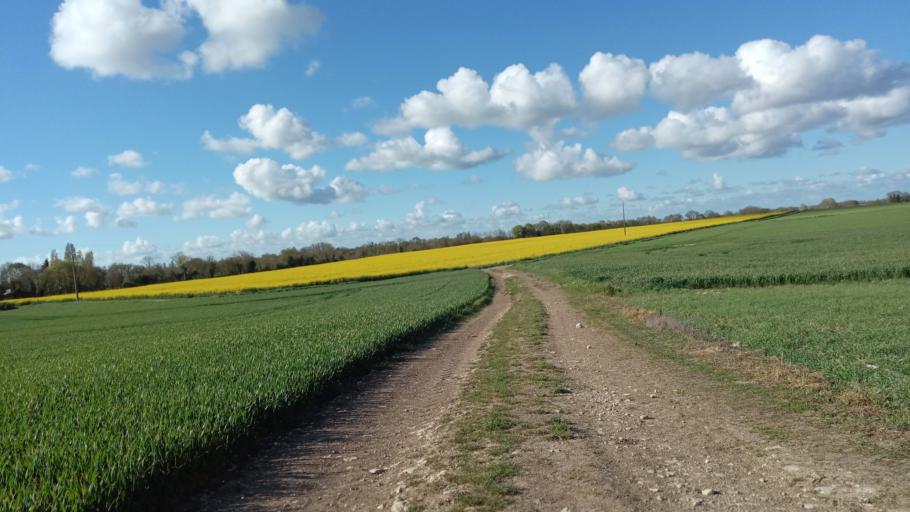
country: FR
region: Poitou-Charentes
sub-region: Departement de la Charente-Maritime
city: Verines
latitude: 46.1663
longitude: -0.9409
